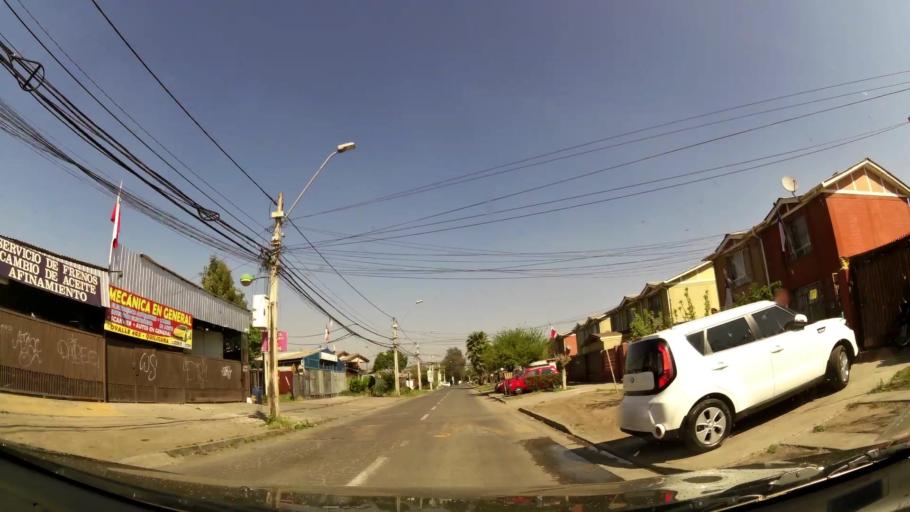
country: CL
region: Santiago Metropolitan
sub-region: Provincia de Santiago
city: Lo Prado
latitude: -33.3507
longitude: -70.7343
